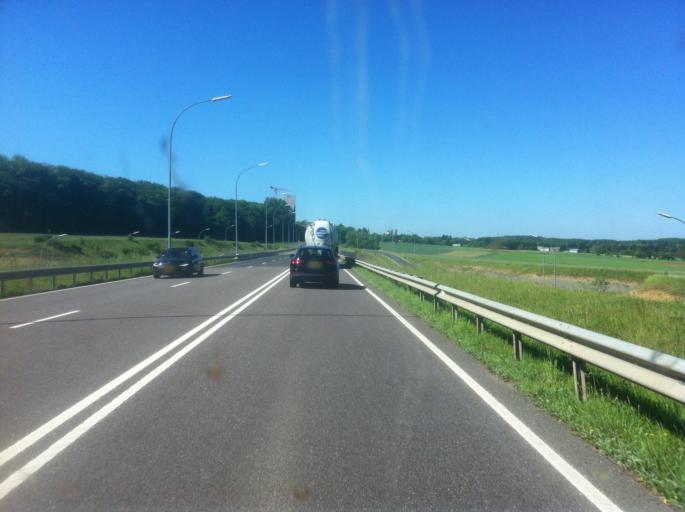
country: LU
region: Grevenmacher
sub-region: Canton d'Echternach
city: Consdorf
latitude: 49.7580
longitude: 6.3417
